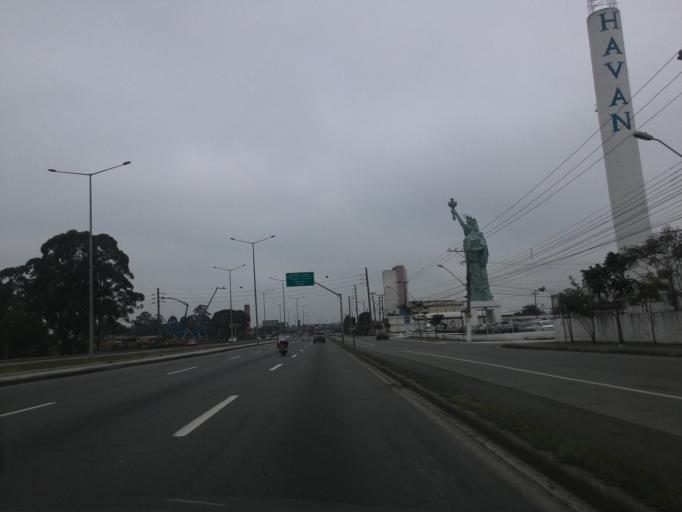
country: BR
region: Parana
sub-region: Curitiba
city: Curitiba
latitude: -25.4628
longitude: -49.2513
